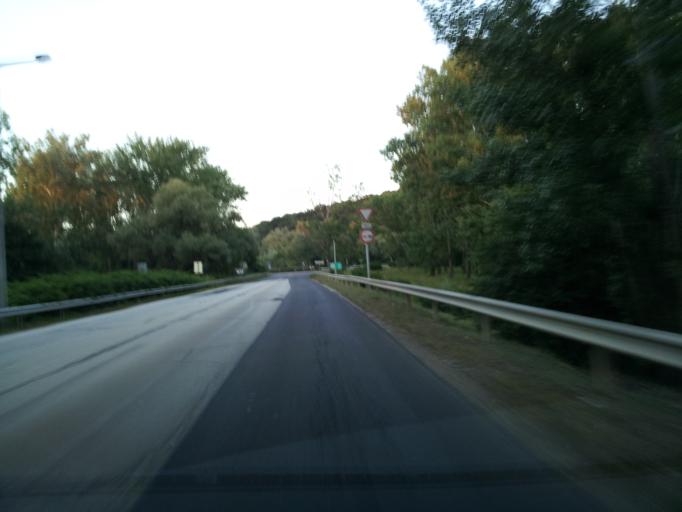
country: HU
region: Komarom-Esztergom
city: Tatabanya
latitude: 47.5684
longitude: 18.4343
